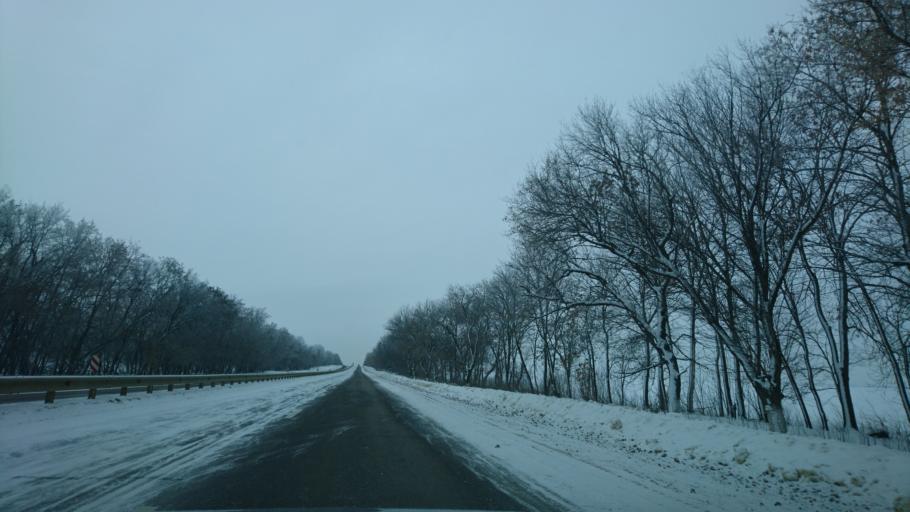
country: RU
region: Belgorod
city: Mayskiy
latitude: 50.4256
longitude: 36.3815
